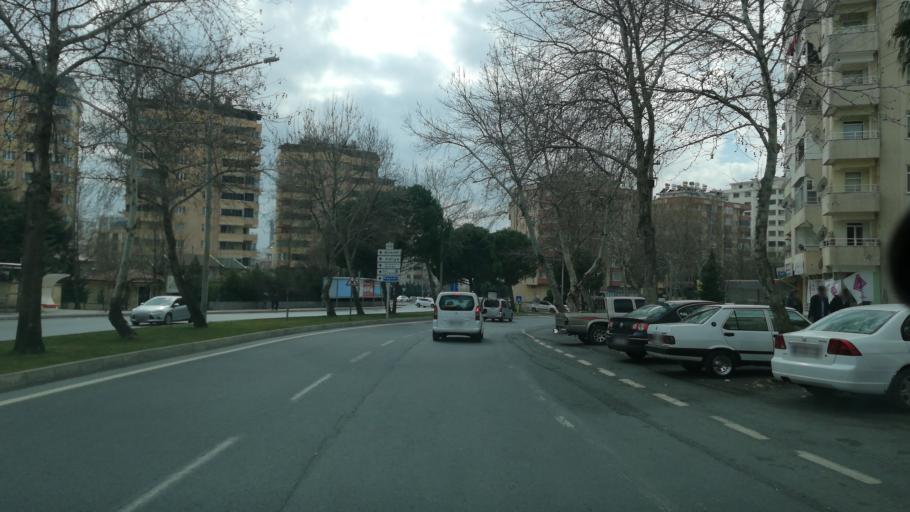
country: TR
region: Kahramanmaras
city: Kahramanmaras
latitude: 37.5856
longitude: 36.8974
